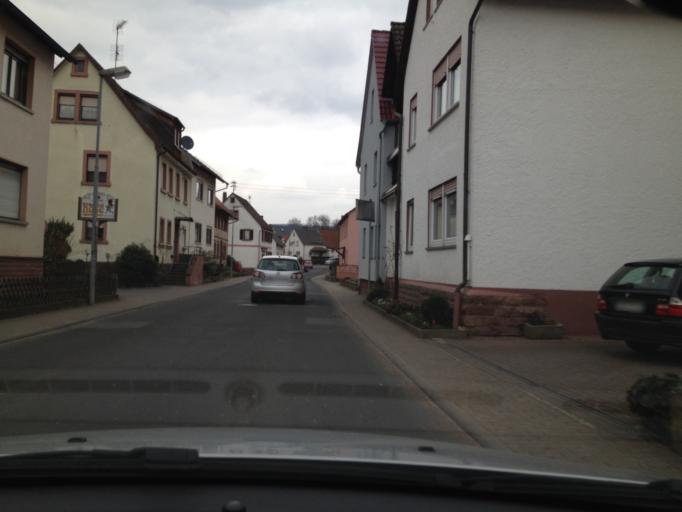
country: DE
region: Bavaria
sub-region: Regierungsbezirk Unterfranken
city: Stadtprozelten
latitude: 49.7645
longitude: 9.4016
